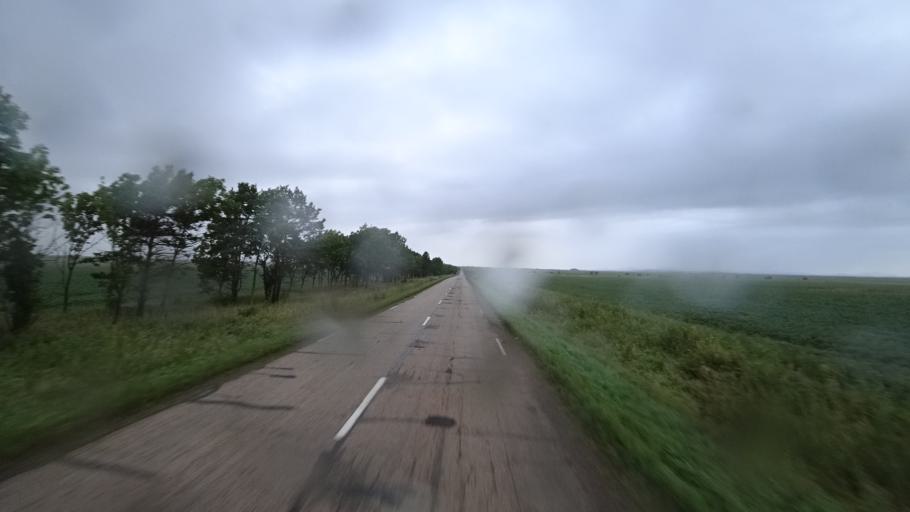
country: RU
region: Primorskiy
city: Chernigovka
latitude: 44.3740
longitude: 132.5298
